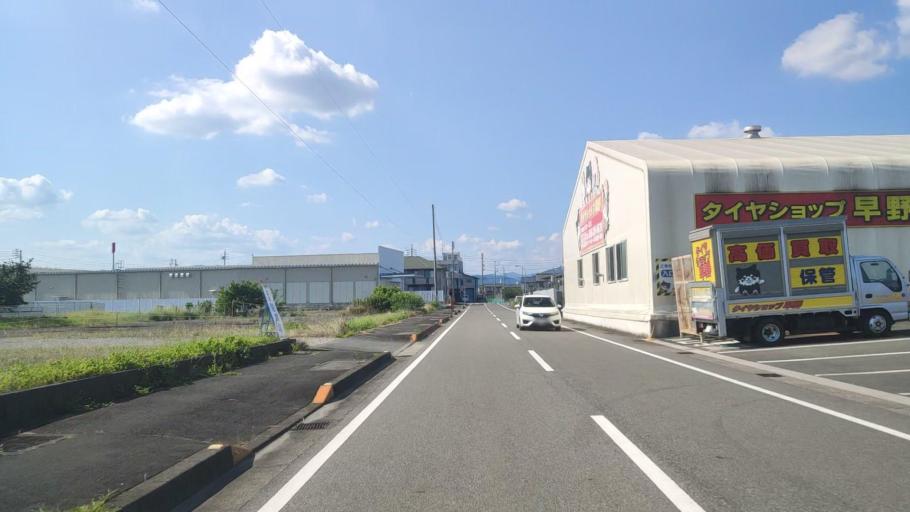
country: JP
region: Gifu
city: Godo
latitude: 35.4486
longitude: 136.6764
